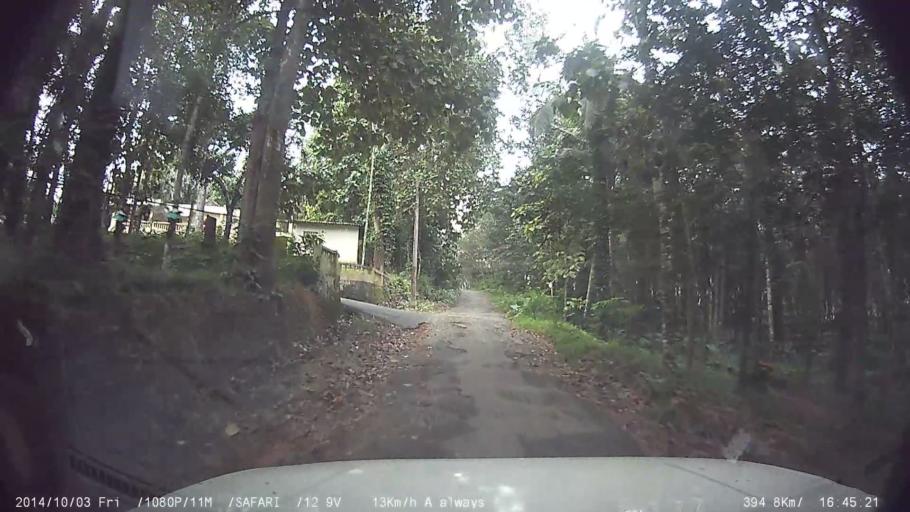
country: IN
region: Kerala
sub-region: Kottayam
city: Palackattumala
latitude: 9.7837
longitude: 76.5770
